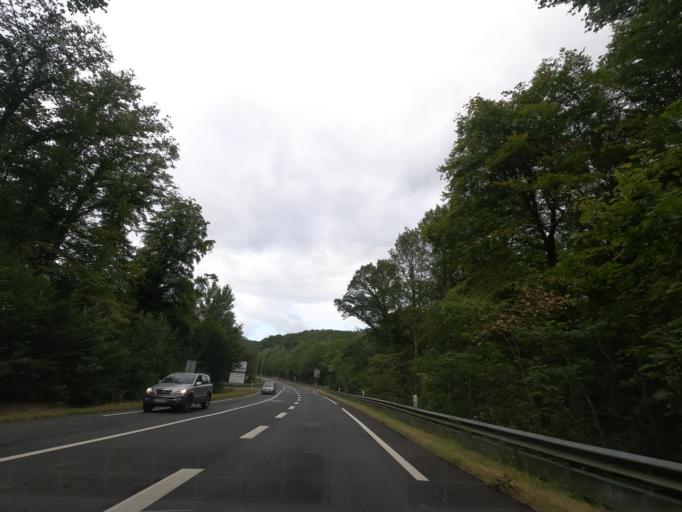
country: FR
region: Haute-Normandie
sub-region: Departement de la Seine-Maritime
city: Sahurs
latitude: 49.3329
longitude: 0.9180
